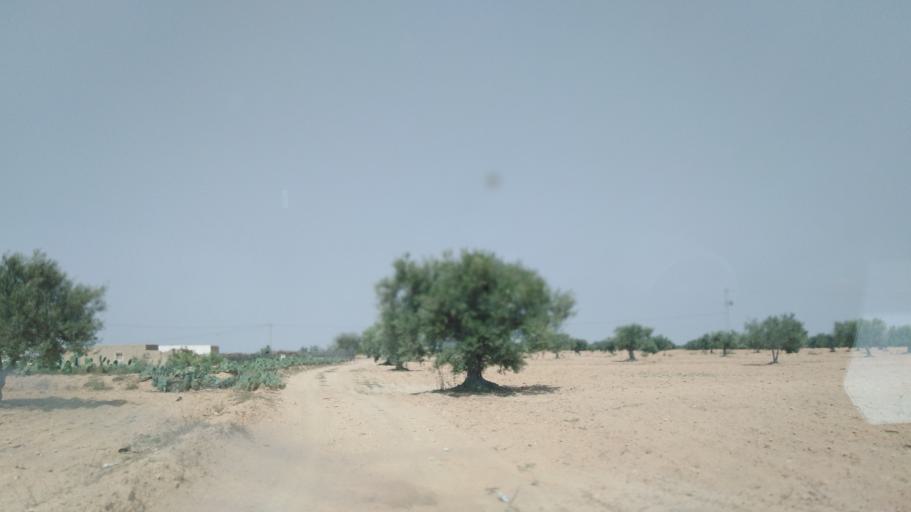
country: TN
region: Safaqis
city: Sfax
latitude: 34.6553
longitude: 10.5551
